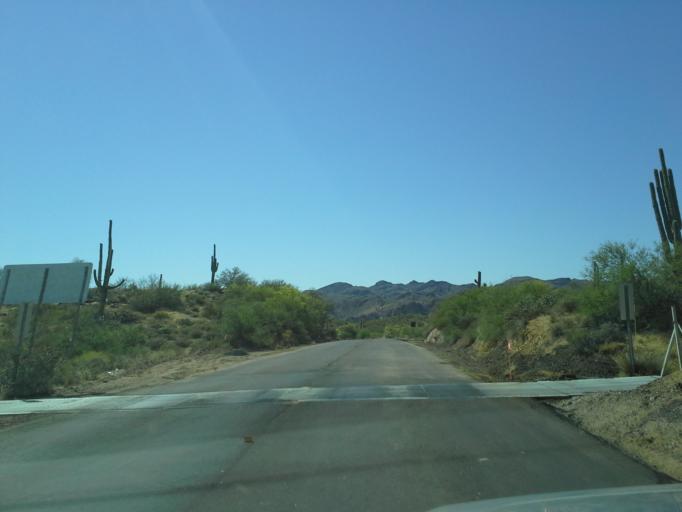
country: US
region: Arizona
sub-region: Pinal County
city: Apache Junction
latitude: 33.5878
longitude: -111.5421
